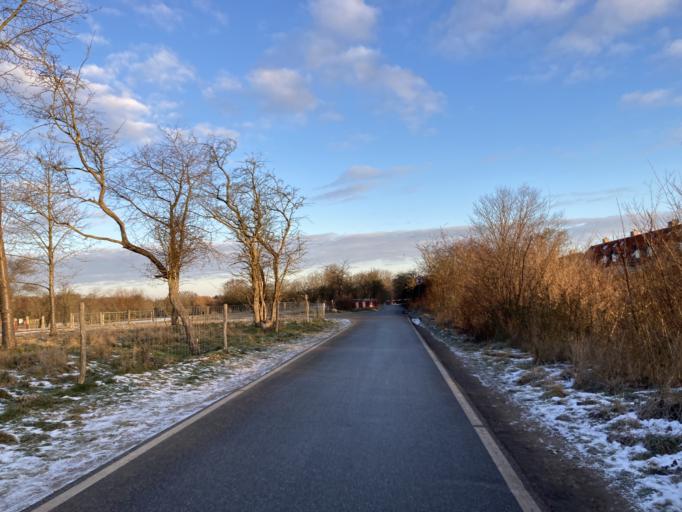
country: DK
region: Capital Region
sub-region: Gladsaxe Municipality
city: Buddinge
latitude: 55.7674
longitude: 12.4761
